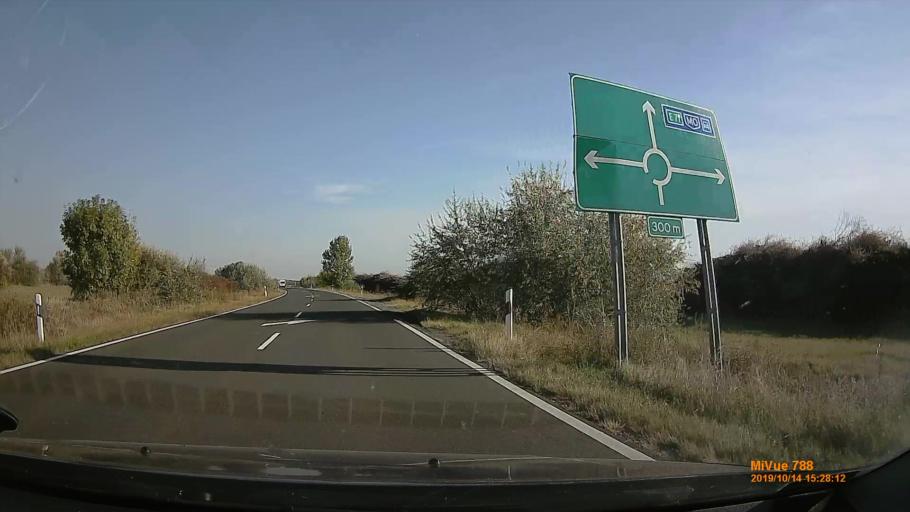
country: HU
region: Pest
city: Ecser
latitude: 47.4331
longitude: 19.3098
